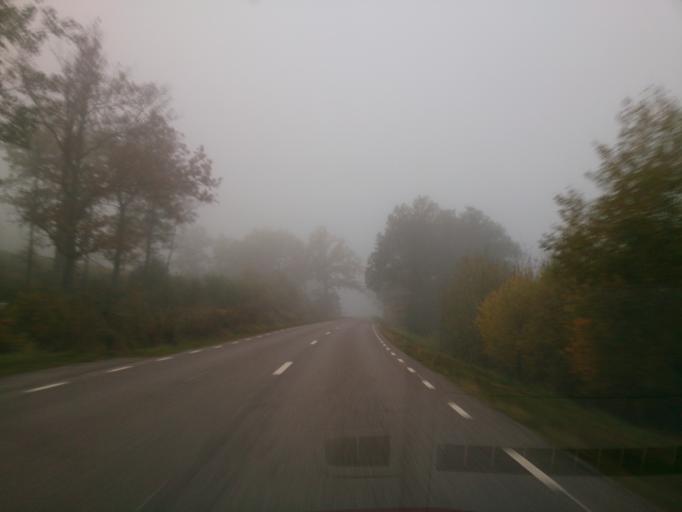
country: SE
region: OEstergoetland
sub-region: Kinda Kommun
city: Rimforsa
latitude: 58.0878
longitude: 15.8360
